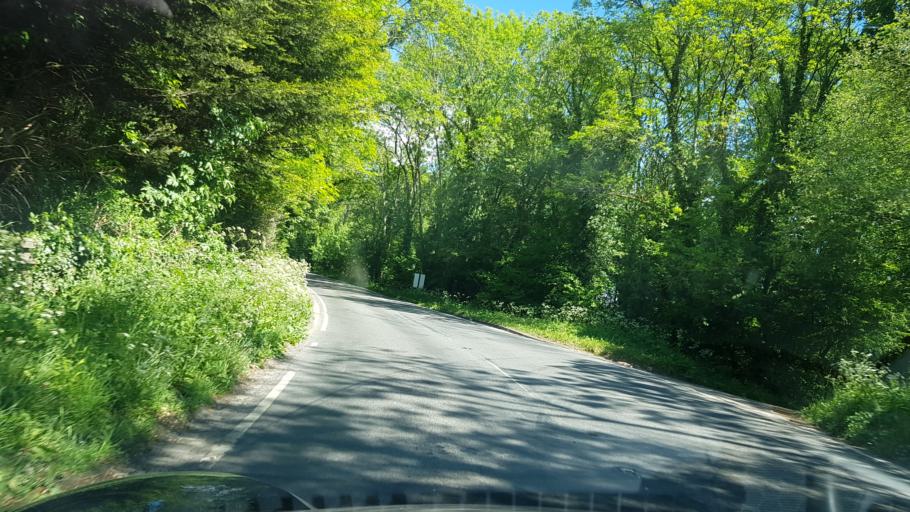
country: GB
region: England
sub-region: Surrey
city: Bramley
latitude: 51.1289
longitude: -0.5541
